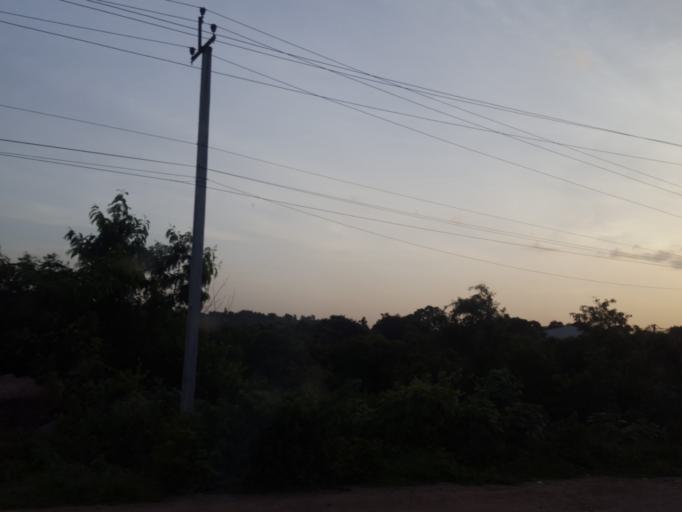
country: IN
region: Telangana
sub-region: Rangareddi
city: Kukatpalli
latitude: 17.5430
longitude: 78.3815
